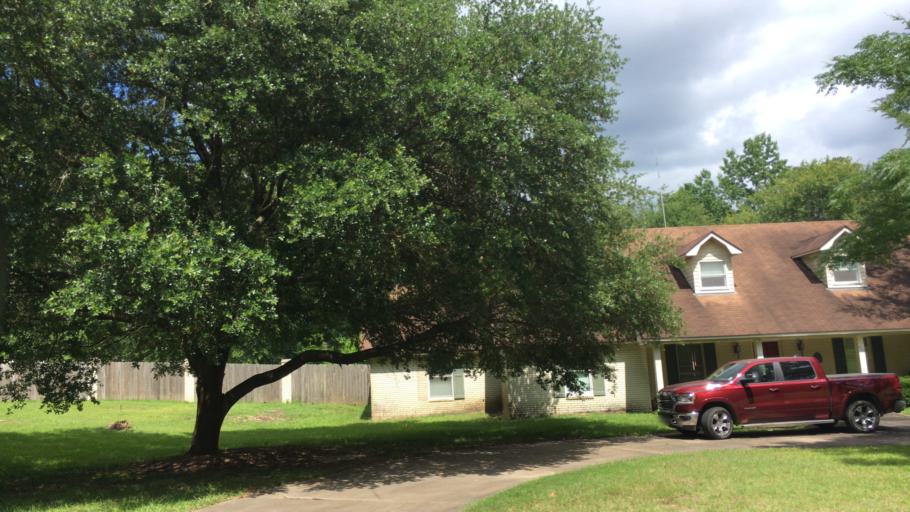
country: US
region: Louisiana
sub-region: Lincoln Parish
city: Ruston
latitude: 32.5493
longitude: -92.6341
